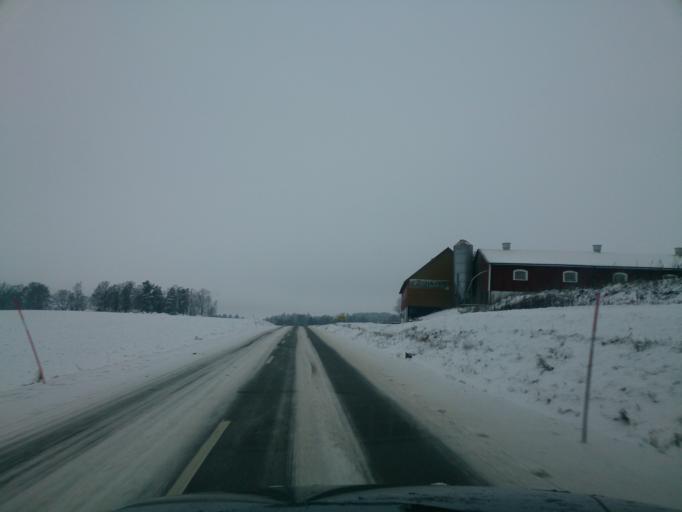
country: SE
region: OEstergoetland
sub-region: Norrkopings Kommun
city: Kimstad
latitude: 58.4082
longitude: 15.9351
